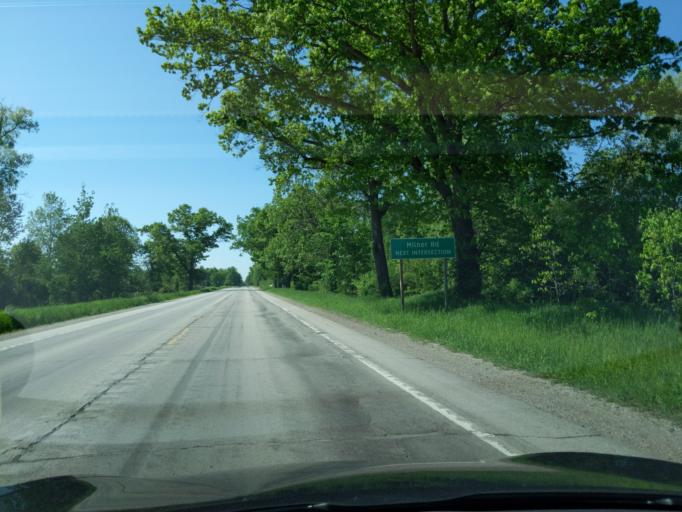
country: US
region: Michigan
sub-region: Ingham County
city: Stockbridge
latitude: 42.4918
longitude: -84.1901
